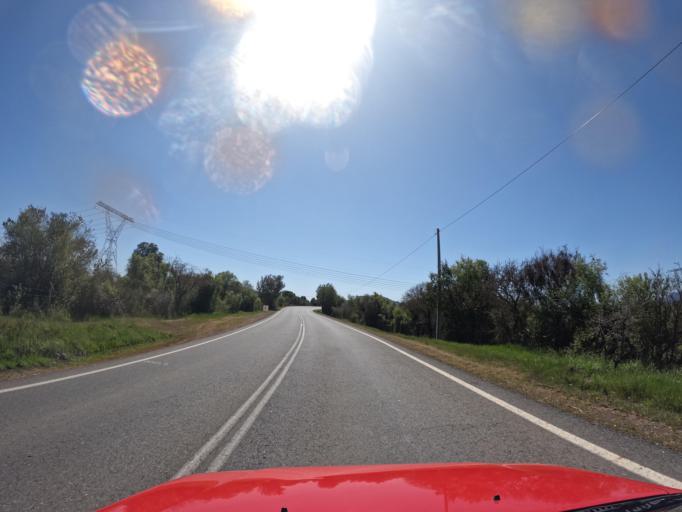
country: CL
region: Maule
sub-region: Provincia de Talca
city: San Clemente
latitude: -35.4794
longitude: -71.2694
